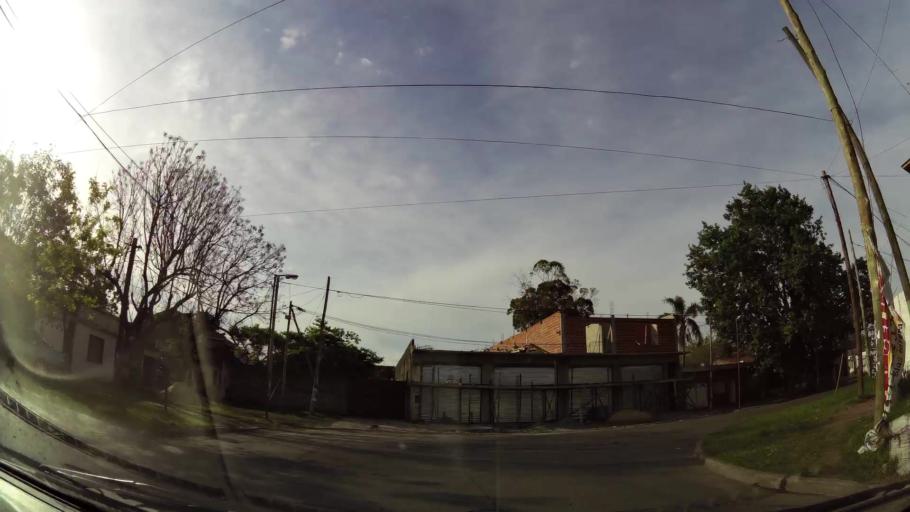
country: AR
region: Buenos Aires
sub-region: Partido de Quilmes
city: Quilmes
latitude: -34.7420
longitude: -58.2603
